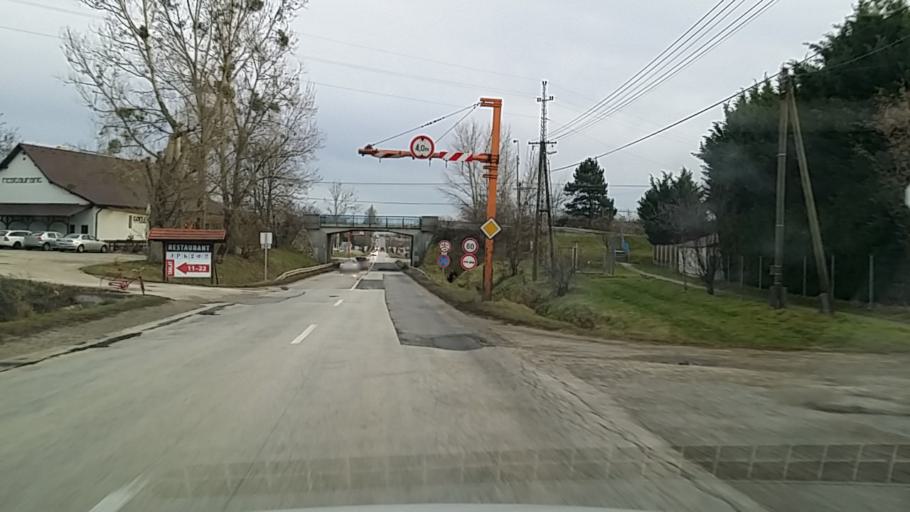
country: HU
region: Fejer
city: Mor
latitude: 47.3696
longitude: 18.1955
